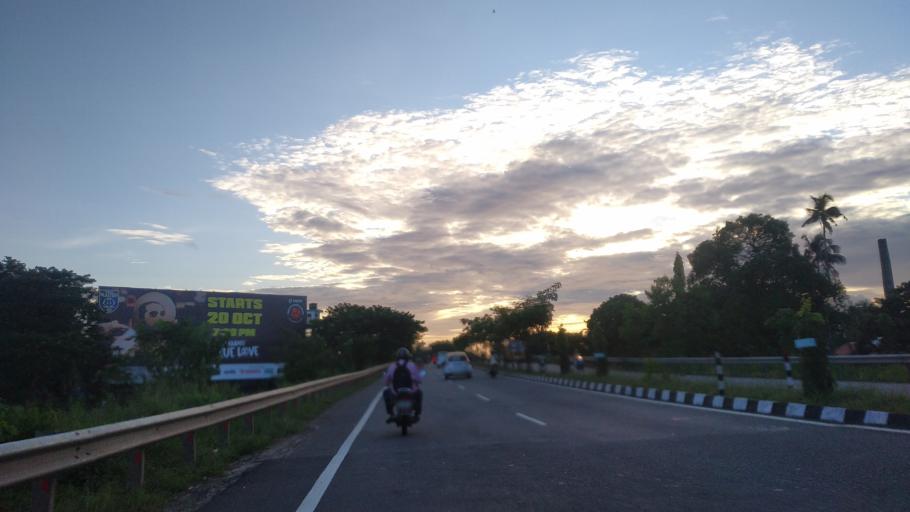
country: IN
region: Kerala
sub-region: Ernakulam
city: Elur
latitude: 10.0649
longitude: 76.2963
